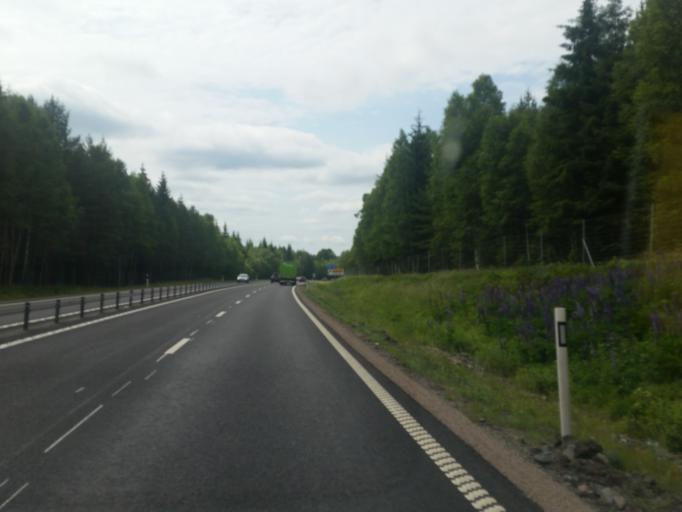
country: SE
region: Dalarna
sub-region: Borlange Kommun
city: Borlaenge
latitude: 60.4429
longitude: 15.3647
